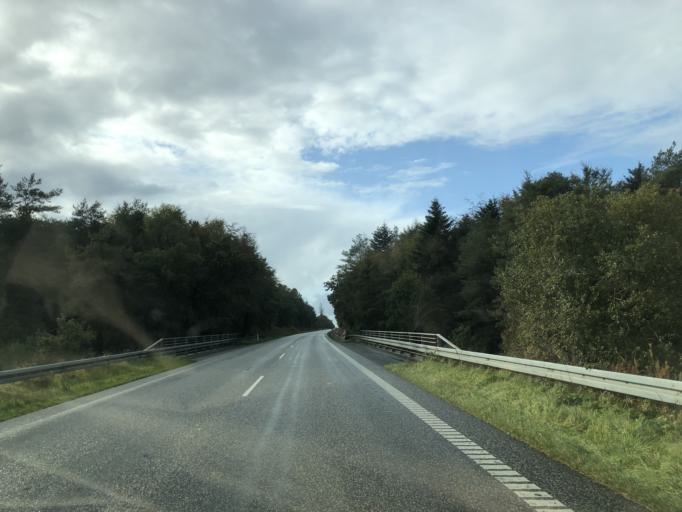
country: DK
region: North Denmark
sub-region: Vesthimmerland Kommune
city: Alestrup
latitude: 56.6111
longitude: 9.4261
